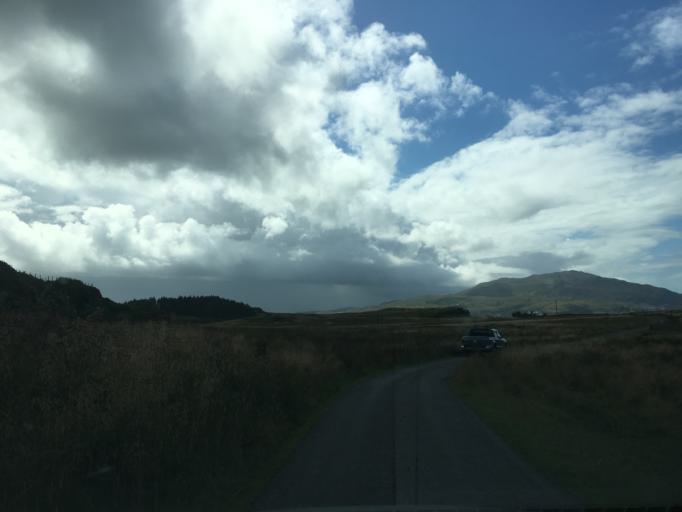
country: GB
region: Scotland
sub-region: Argyll and Bute
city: Isle Of Mull
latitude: 56.2198
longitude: -5.6491
